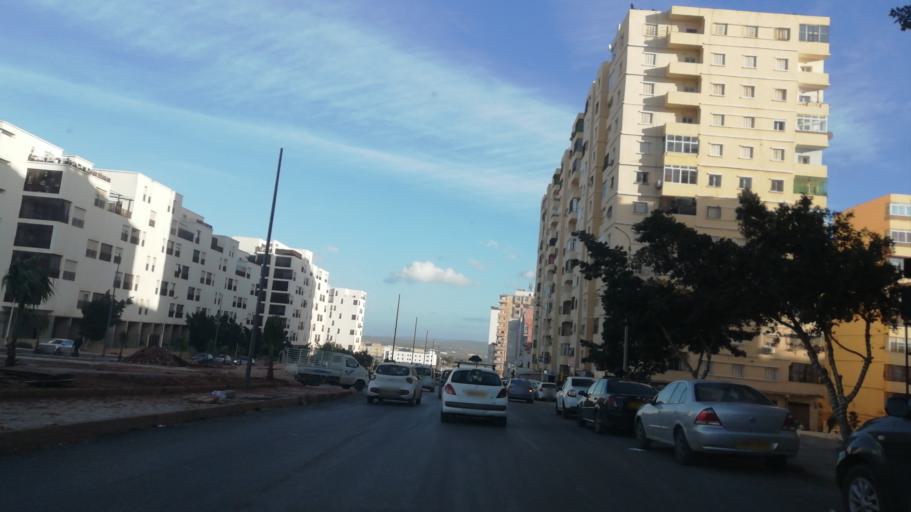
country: DZ
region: Oran
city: Bir el Djir
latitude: 35.7063
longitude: -0.5585
